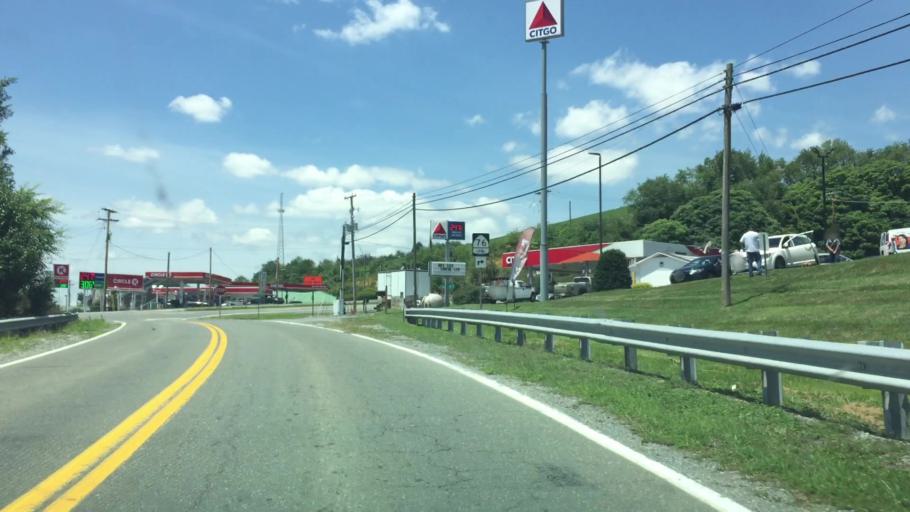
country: US
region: Virginia
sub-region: Wythe County
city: Wytheville
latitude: 36.9468
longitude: -80.9486
